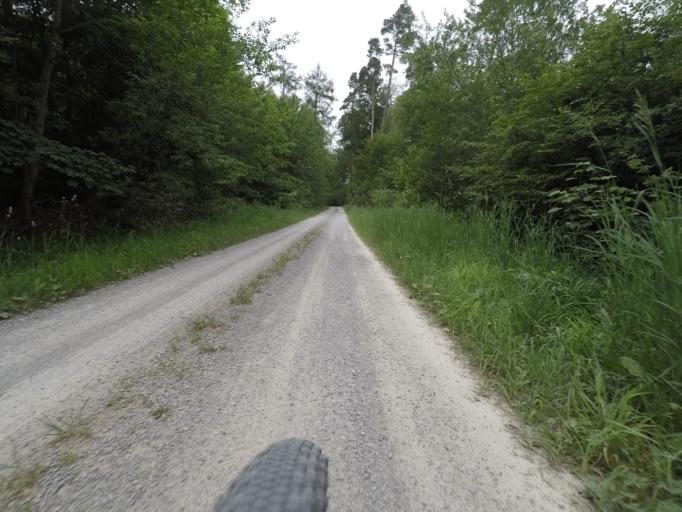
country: DE
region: Baden-Wuerttemberg
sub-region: Regierungsbezirk Stuttgart
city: Hildrizhausen
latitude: 48.5751
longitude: 8.9754
